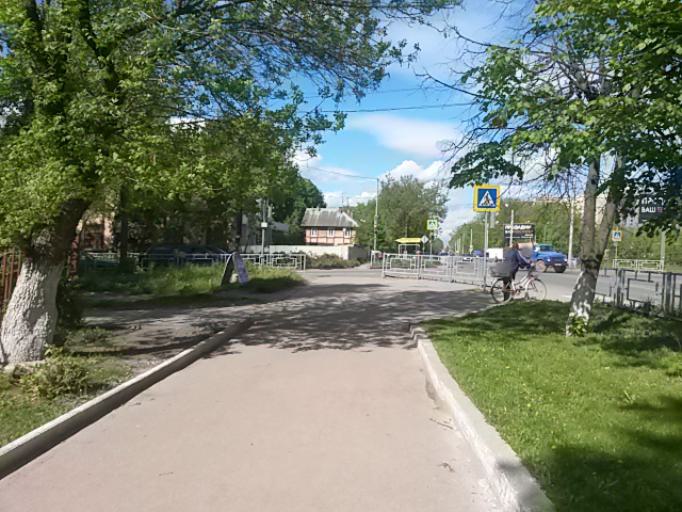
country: RU
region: Ivanovo
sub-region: Gorod Ivanovo
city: Ivanovo
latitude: 57.0024
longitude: 40.9442
